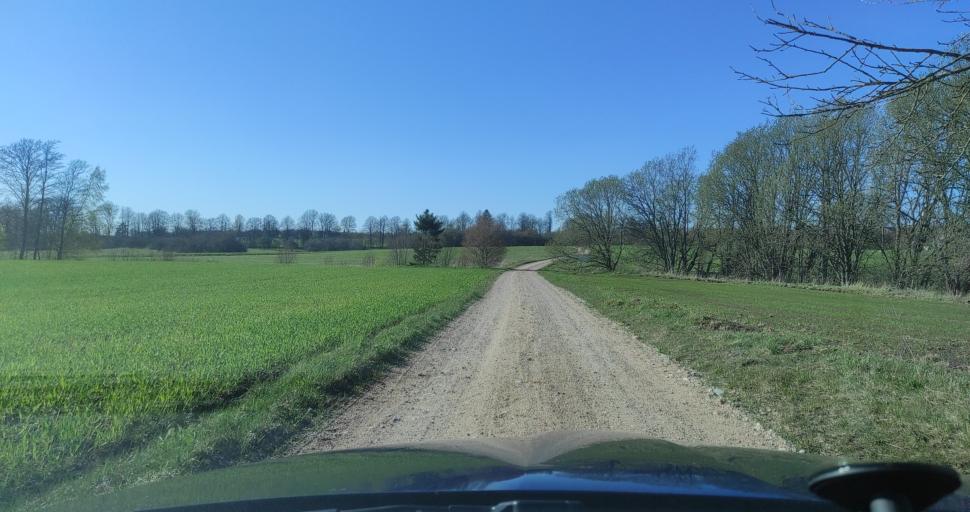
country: LV
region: Kuldigas Rajons
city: Kuldiga
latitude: 56.8745
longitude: 21.8360
